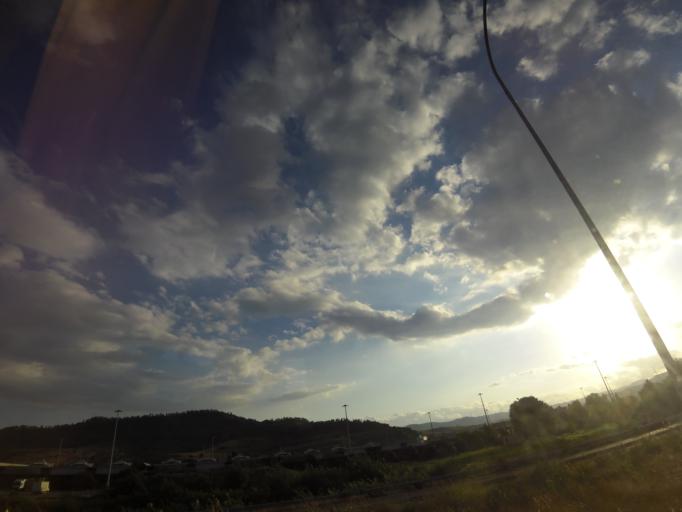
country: IT
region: Calabria
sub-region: Provincia di Catanzaro
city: Catanzaro
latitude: 38.8566
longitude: 16.5732
